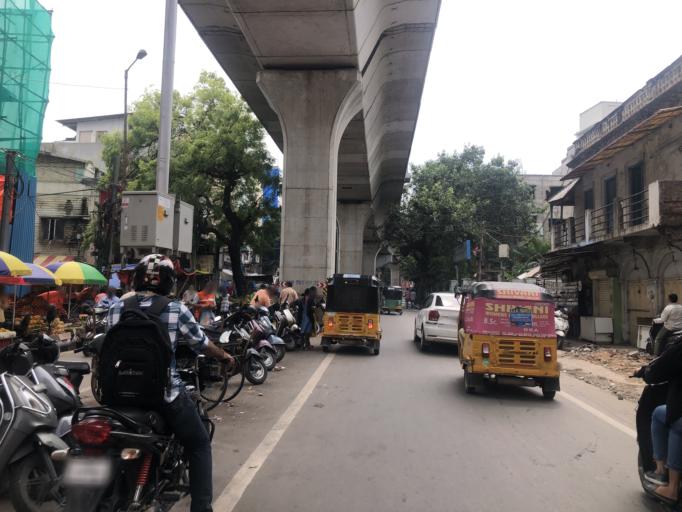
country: IN
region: Telangana
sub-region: Hyderabad
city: Hyderabad
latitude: 17.3888
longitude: 78.4879
